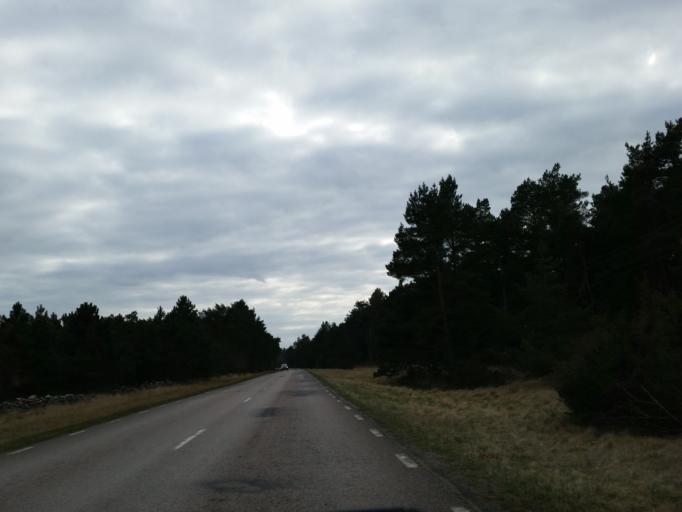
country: SE
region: Kalmar
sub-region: Morbylanga Kommun
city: Sodra Sandby
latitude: 56.5839
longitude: 16.6237
